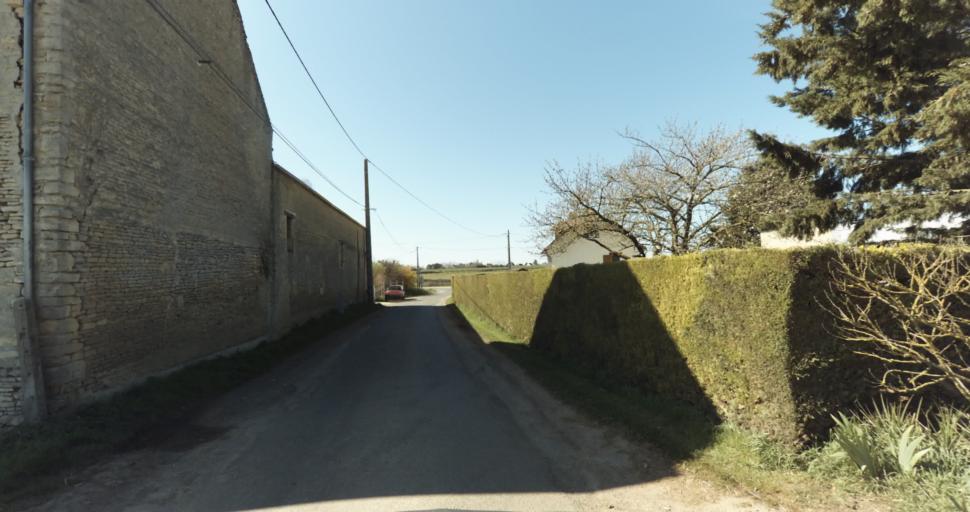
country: FR
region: Lower Normandy
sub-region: Departement du Calvados
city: Saint-Pierre-sur-Dives
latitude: 49.0520
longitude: -0.0494
